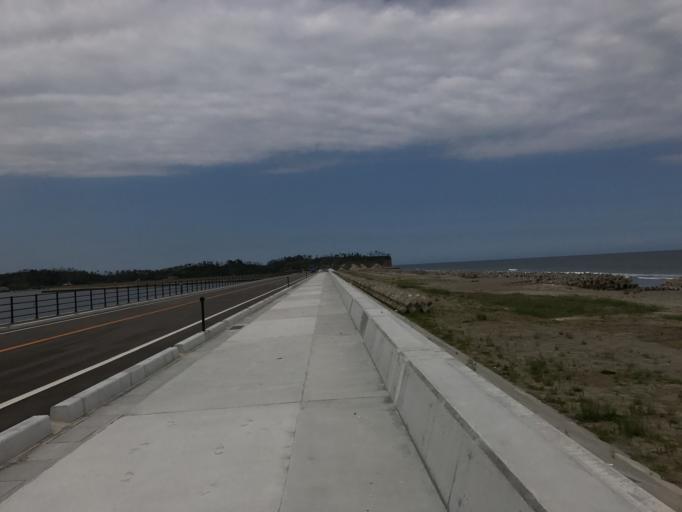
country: JP
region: Miyagi
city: Marumori
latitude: 37.8127
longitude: 140.9855
